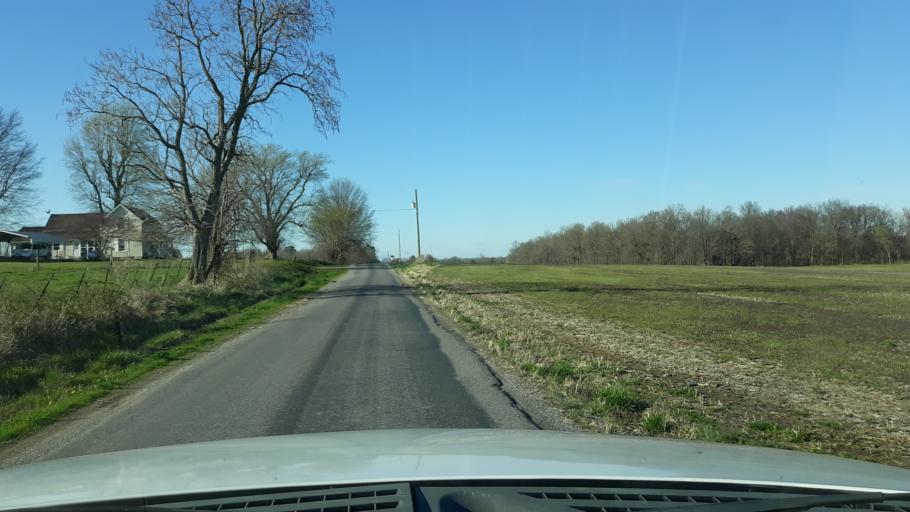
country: US
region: Illinois
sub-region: Saline County
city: Harrisburg
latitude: 37.7878
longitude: -88.6056
